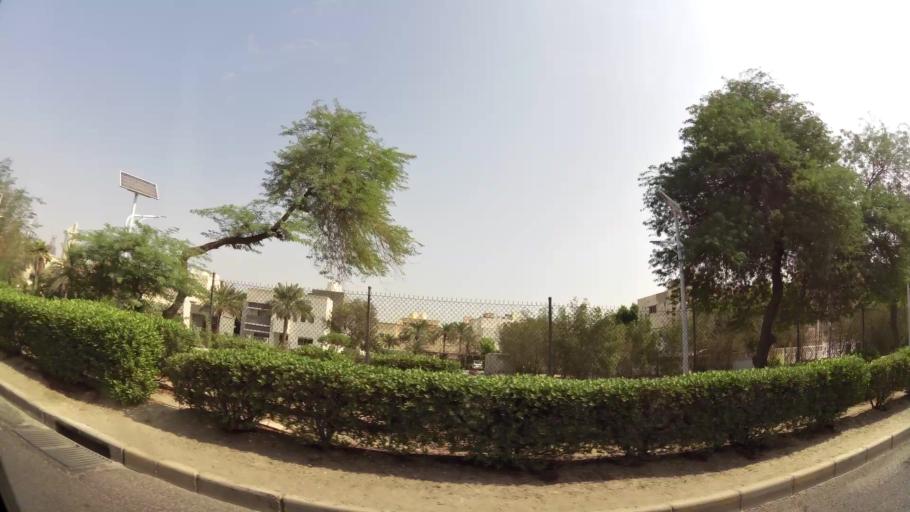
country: KW
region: Al Asimah
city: Ad Dasmah
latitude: 29.3584
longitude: 47.9889
